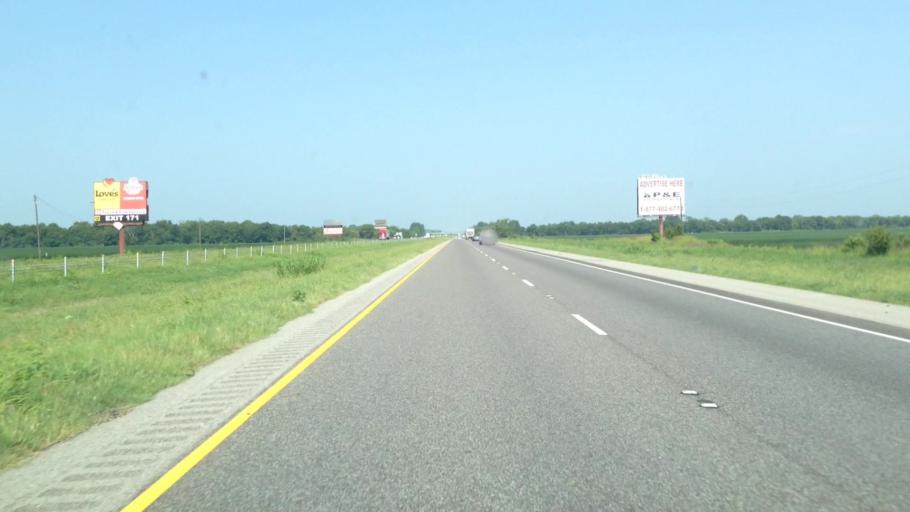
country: US
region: Mississippi
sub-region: Warren County
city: Vicksburg
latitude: 32.3264
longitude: -91.0020
